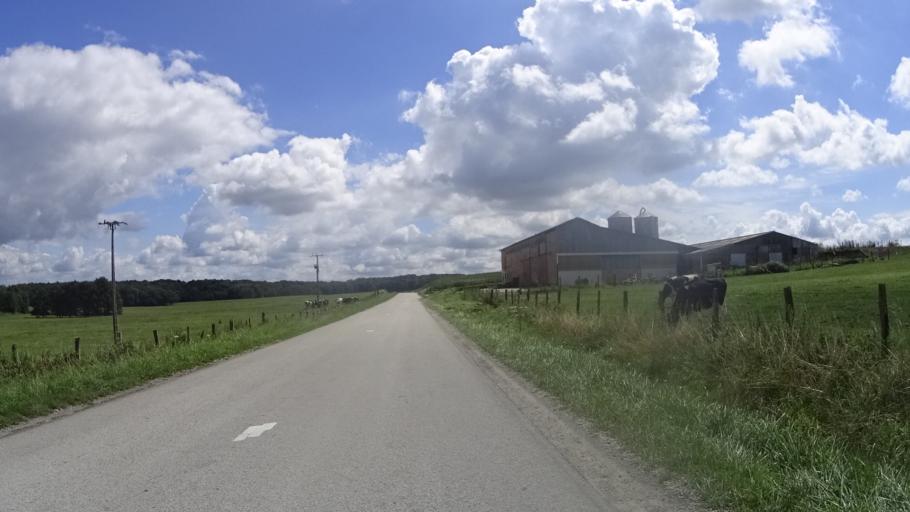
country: FR
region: Champagne-Ardenne
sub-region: Departement de la Haute-Marne
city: Montier-en-Der
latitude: 48.4599
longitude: 4.7154
